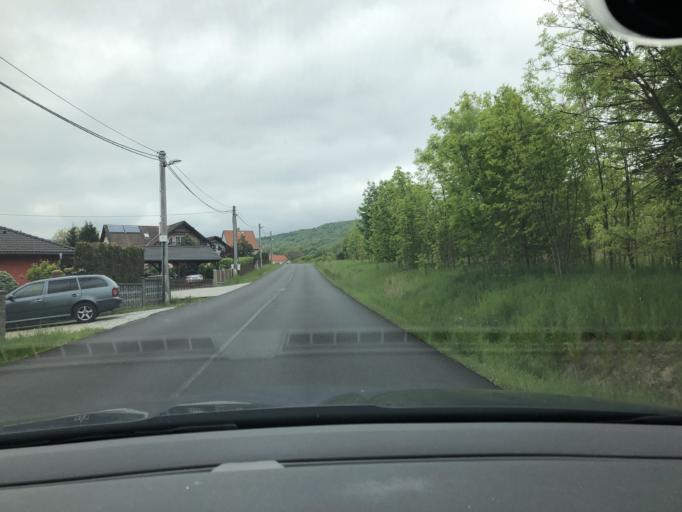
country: CZ
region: Ustecky
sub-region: Okres Usti nad Labem
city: Usti nad Labem
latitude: 50.7021
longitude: 14.0168
